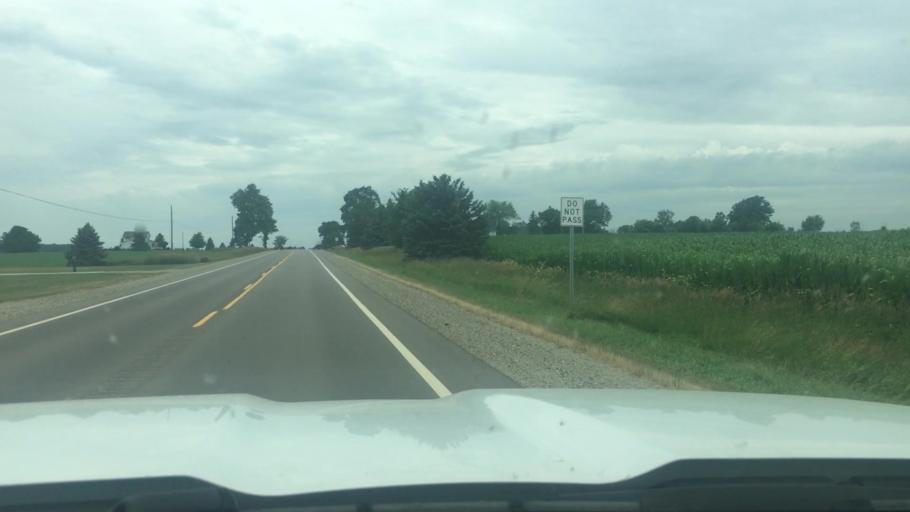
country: US
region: Michigan
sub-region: Clinton County
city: Fowler
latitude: 43.0017
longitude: -84.7040
